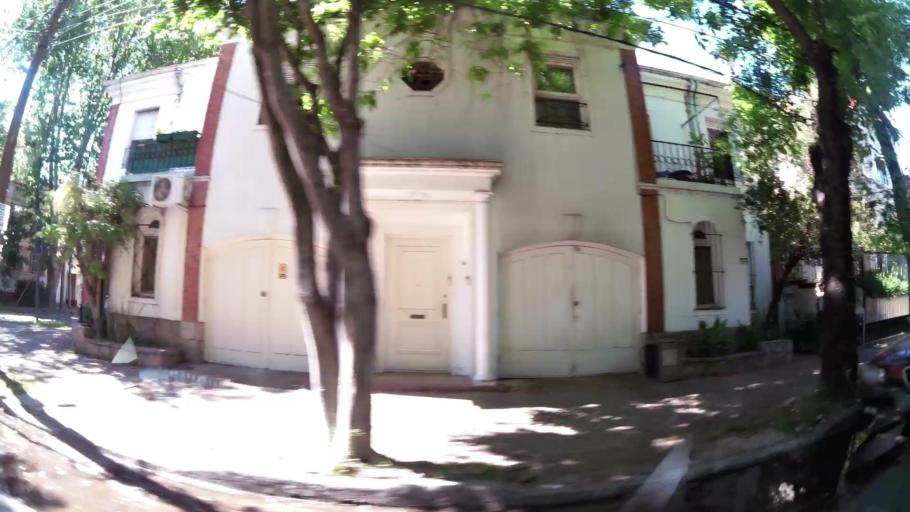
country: AR
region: Buenos Aires
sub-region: Partido de Vicente Lopez
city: Olivos
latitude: -34.5281
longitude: -58.4772
